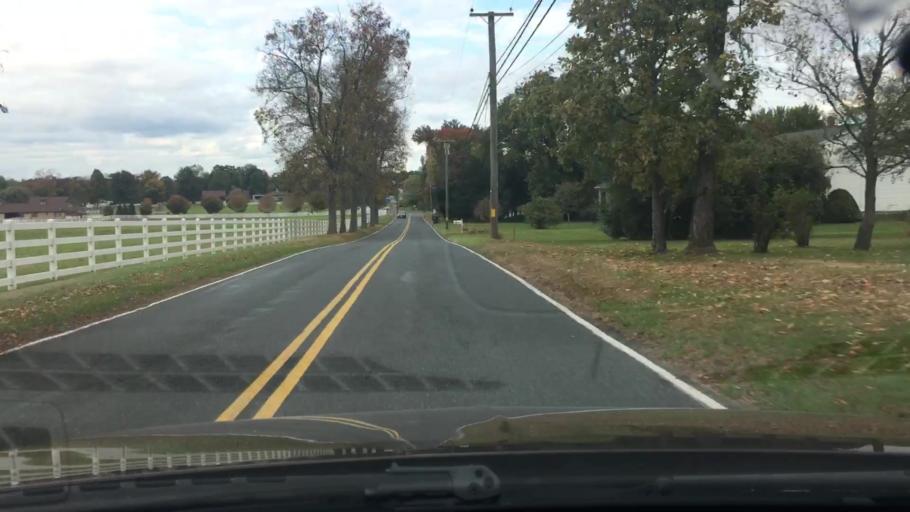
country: US
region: Connecticut
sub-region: Tolland County
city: Somers
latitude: 41.9749
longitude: -72.4843
